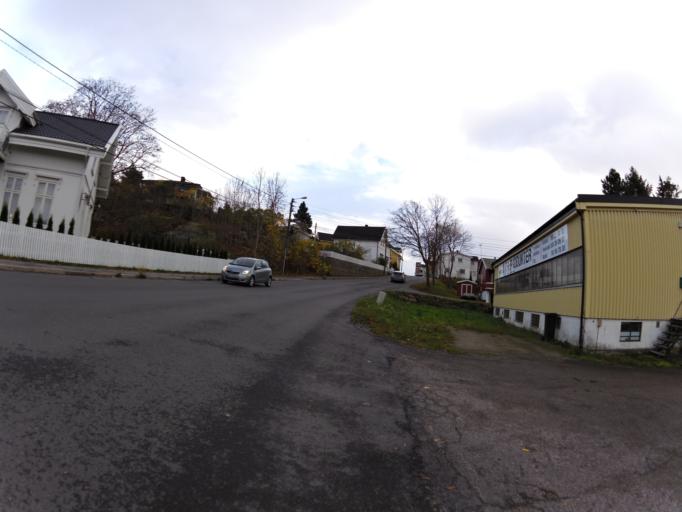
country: NO
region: Ostfold
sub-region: Fredrikstad
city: Fredrikstad
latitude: 59.2292
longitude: 10.9178
